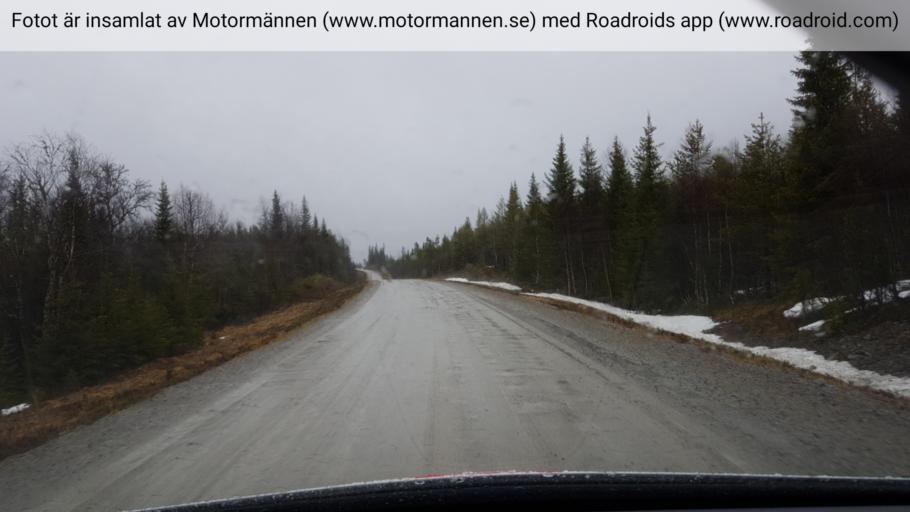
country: SE
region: Jaemtland
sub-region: Are Kommun
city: Are
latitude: 62.6302
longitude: 13.1100
